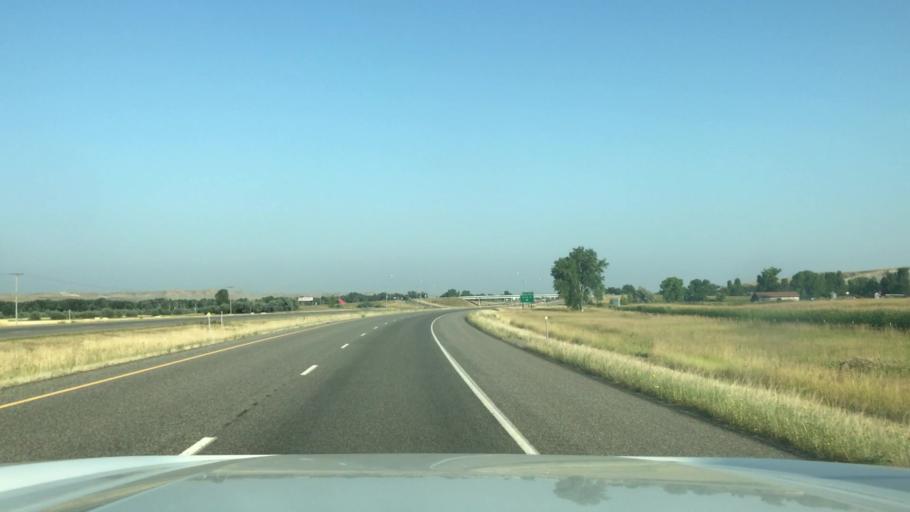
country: US
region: Montana
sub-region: Big Horn County
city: Hardin
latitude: 45.7452
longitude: -107.5885
